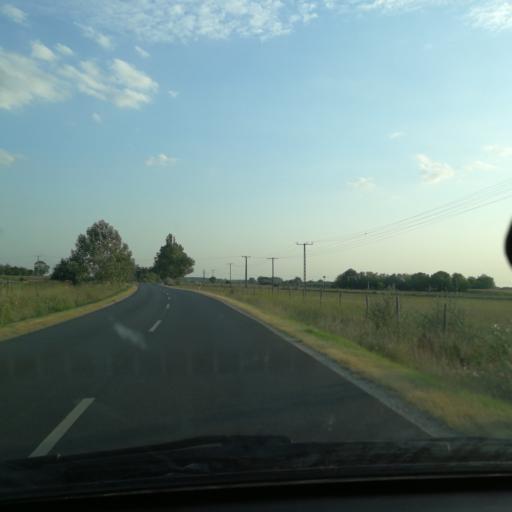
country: HU
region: Bacs-Kiskun
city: Kiskunmajsa
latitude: 46.4843
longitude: 19.7146
